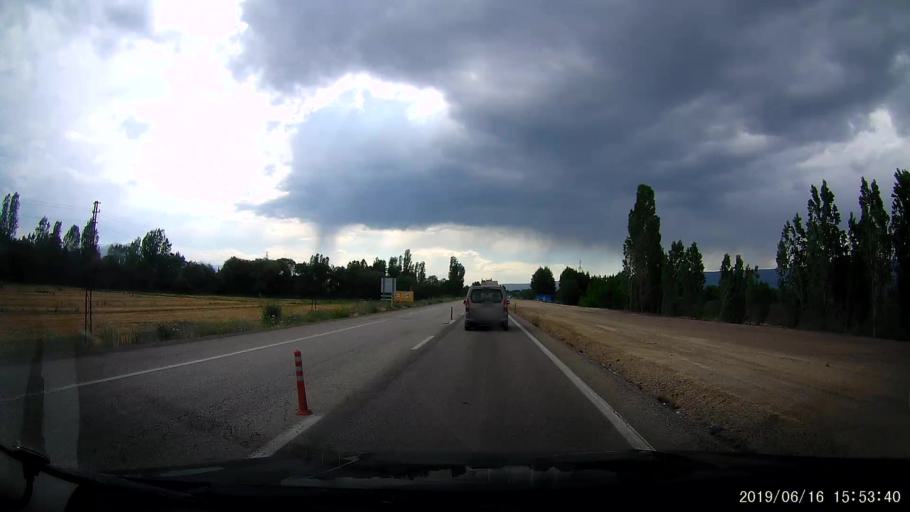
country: TR
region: Erzurum
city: Pasinler
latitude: 39.9775
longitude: 41.6440
